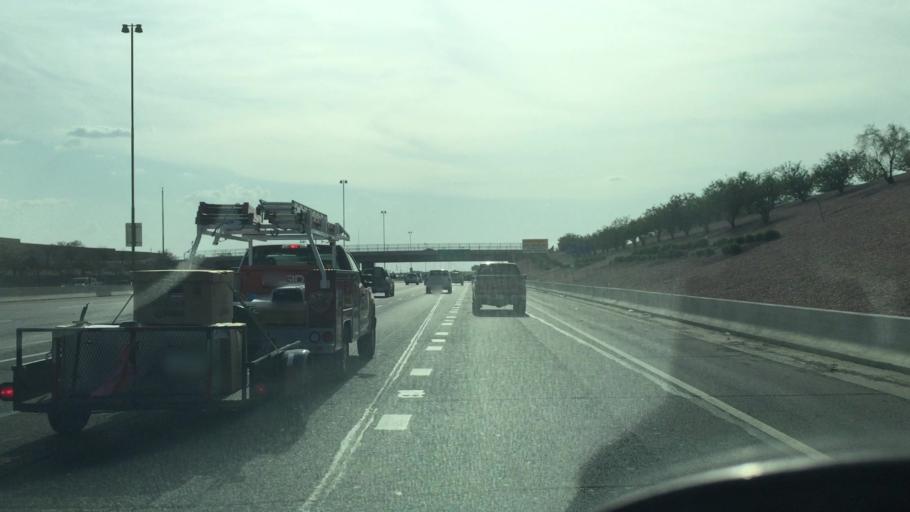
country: US
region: Arizona
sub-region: Maricopa County
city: Gilbert
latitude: 33.3854
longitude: -111.7975
